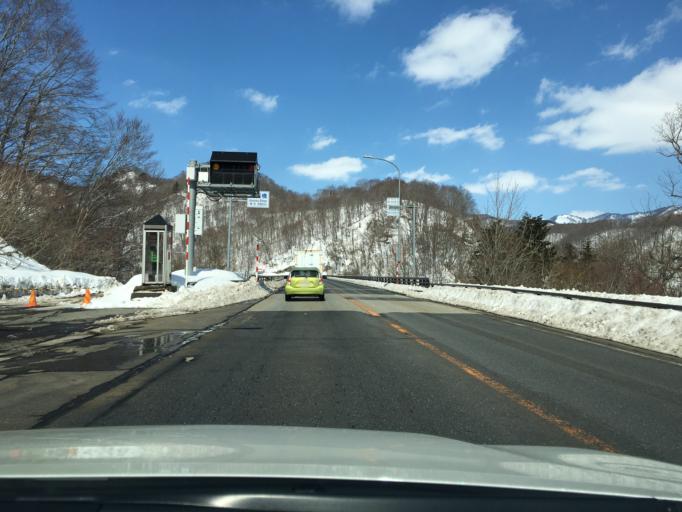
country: JP
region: Yamagata
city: Sagae
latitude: 38.4619
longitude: 139.9912
